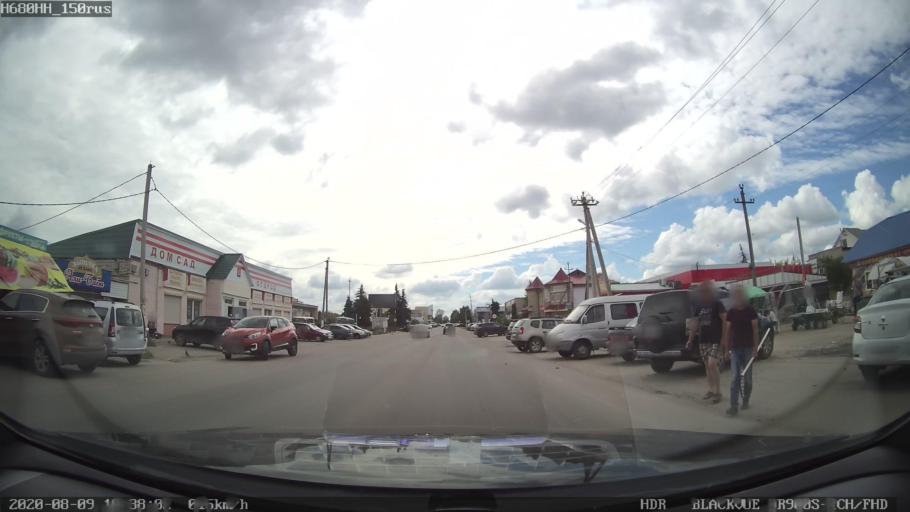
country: RU
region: Tula
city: Zaokskiy
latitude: 54.7357
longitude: 37.3983
